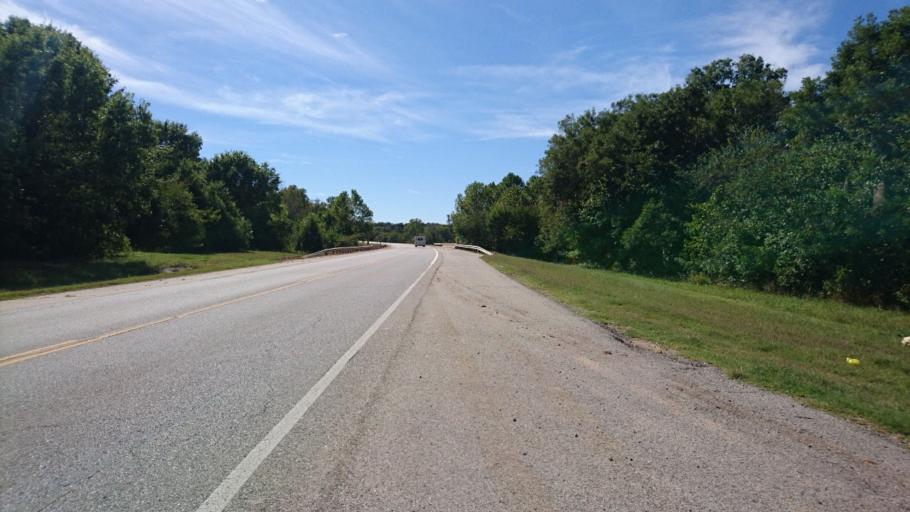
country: US
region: Oklahoma
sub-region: Lincoln County
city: Stroud
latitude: 35.7383
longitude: -96.7160
